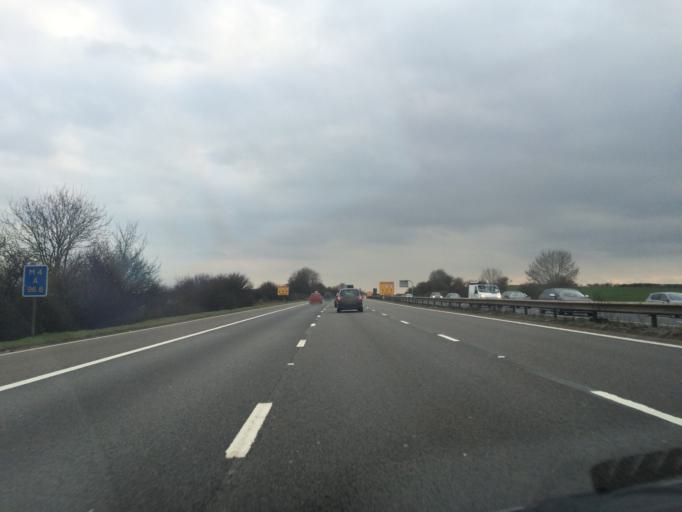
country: GB
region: England
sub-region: West Berkshire
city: Winterbourne
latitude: 51.4536
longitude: -1.3784
